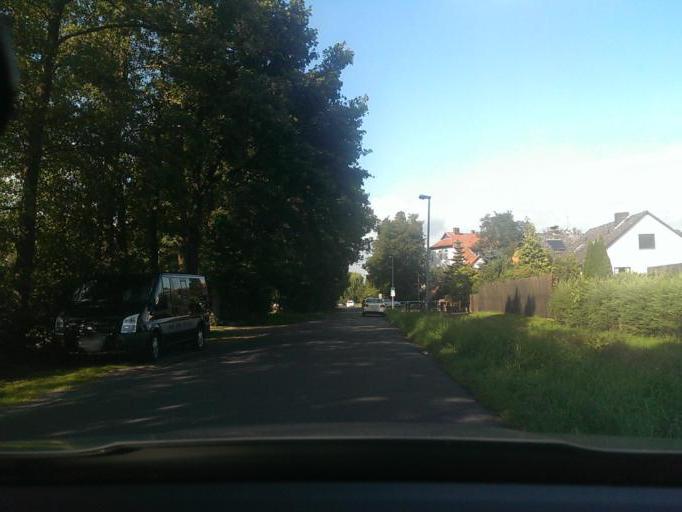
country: DE
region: Lower Saxony
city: Elze
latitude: 52.5500
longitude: 9.7637
